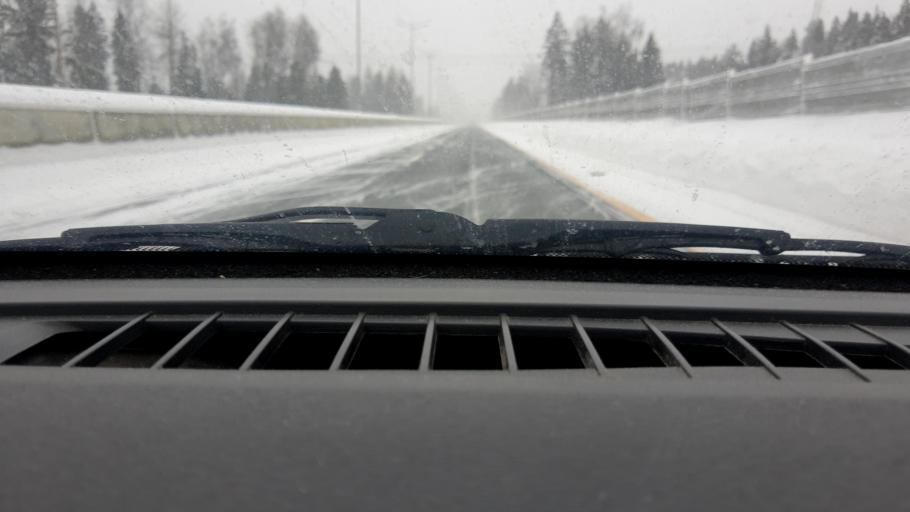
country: RU
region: Moskovskaya
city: Krasnoarmeysk
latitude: 56.0541
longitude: 38.1314
